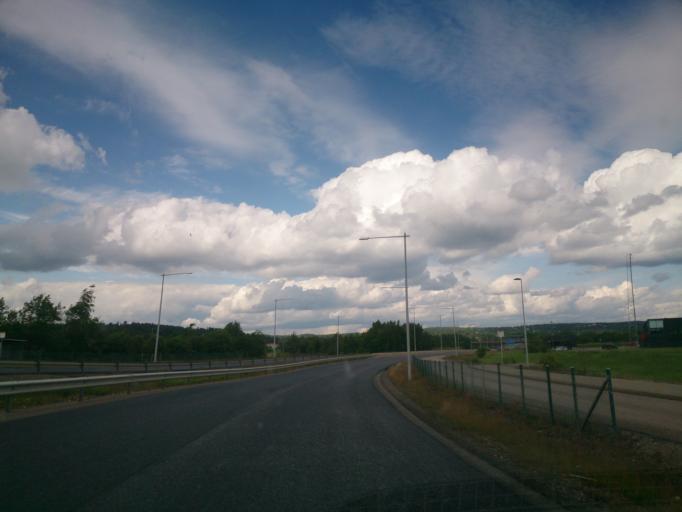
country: SE
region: OEstergoetland
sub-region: Norrkopings Kommun
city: Jursla
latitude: 58.6453
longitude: 16.1635
